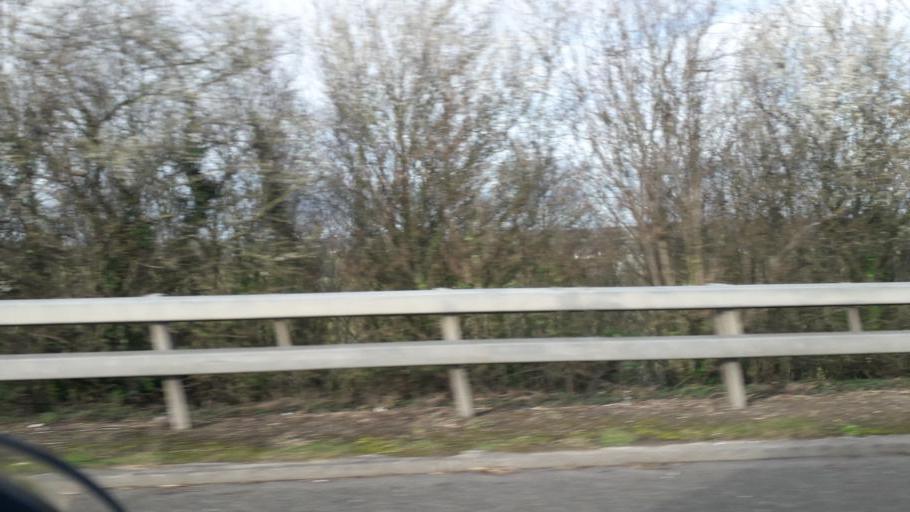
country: IE
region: Leinster
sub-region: Lu
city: Dunleer
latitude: 53.8010
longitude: -6.3999
